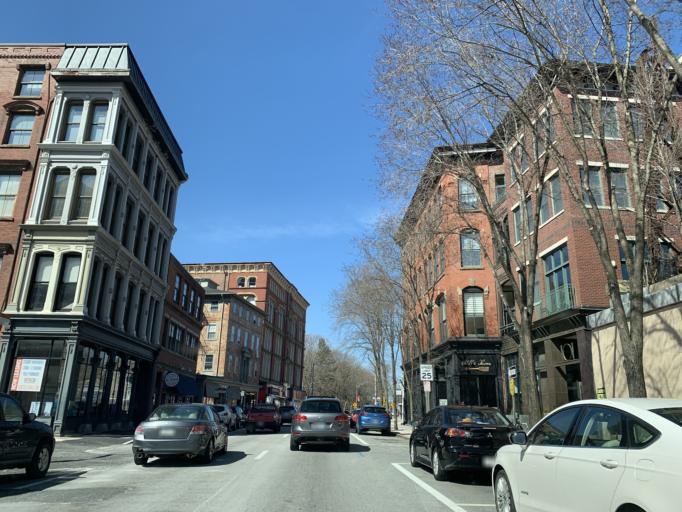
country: US
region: Rhode Island
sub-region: Providence County
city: Providence
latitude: 41.8277
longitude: -71.4092
